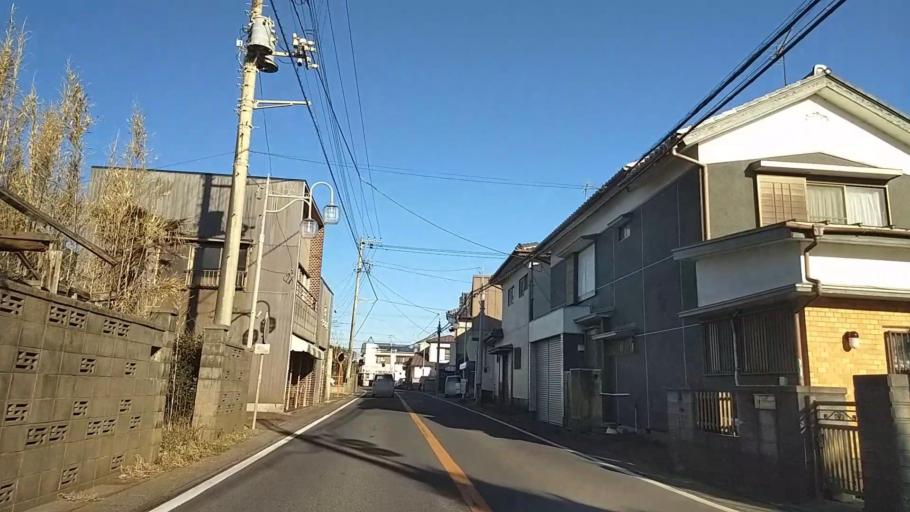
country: JP
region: Chiba
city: Asahi
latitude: 35.6944
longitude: 140.6661
